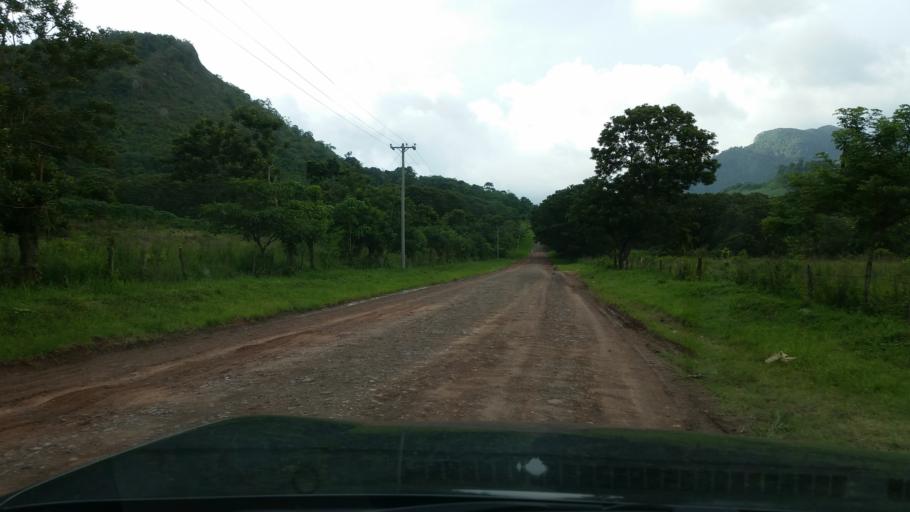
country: NI
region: Jinotega
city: Jinotega
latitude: 13.2206
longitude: -85.7311
